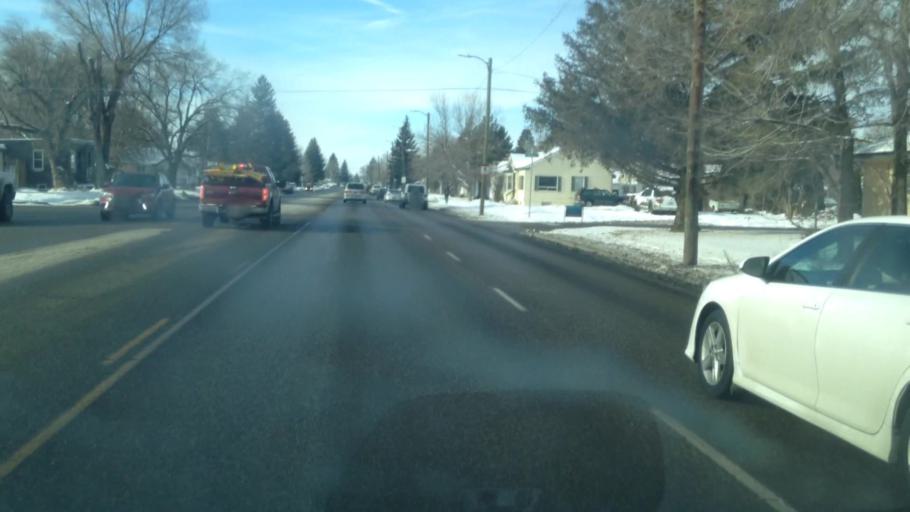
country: US
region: Idaho
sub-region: Bonneville County
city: Idaho Falls
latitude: 43.4826
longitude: -112.0256
